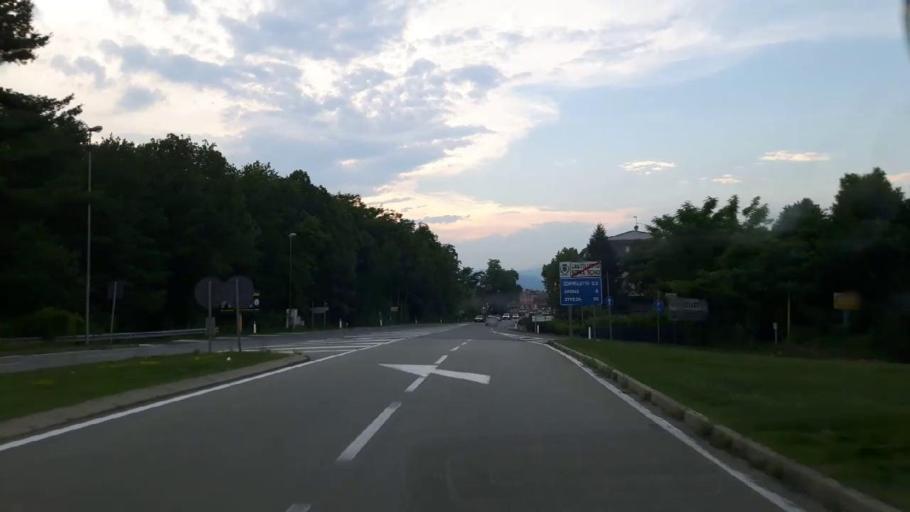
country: IT
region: Piedmont
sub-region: Provincia di Novara
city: Comignago
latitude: 45.7204
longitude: 8.5853
